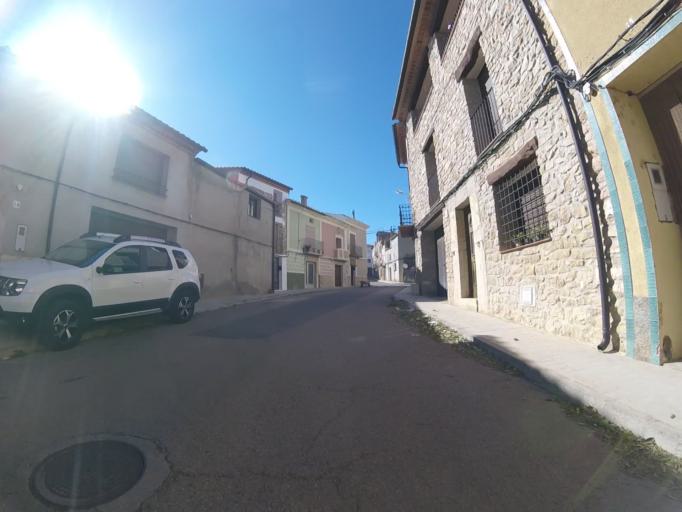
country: ES
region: Valencia
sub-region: Provincia de Castello
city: Cati
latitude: 40.4251
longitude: 0.0787
